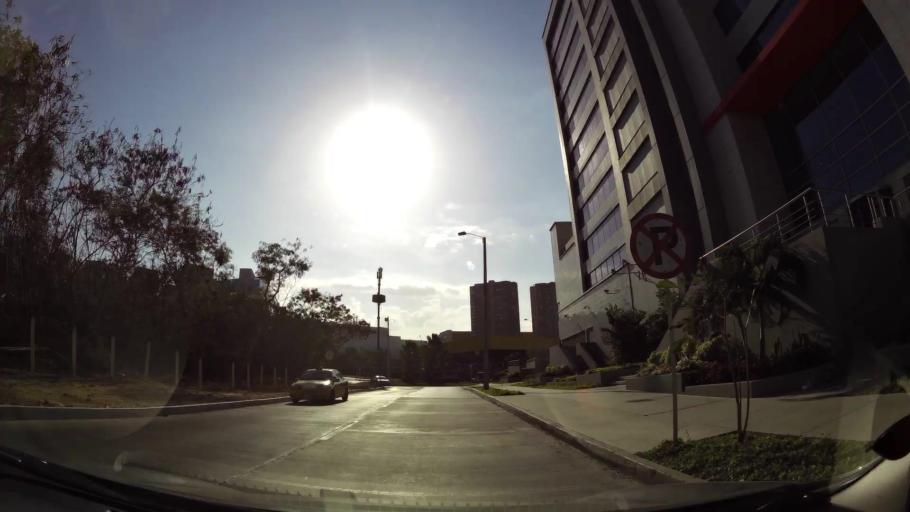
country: CO
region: Atlantico
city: Barranquilla
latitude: 11.0167
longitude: -74.8311
